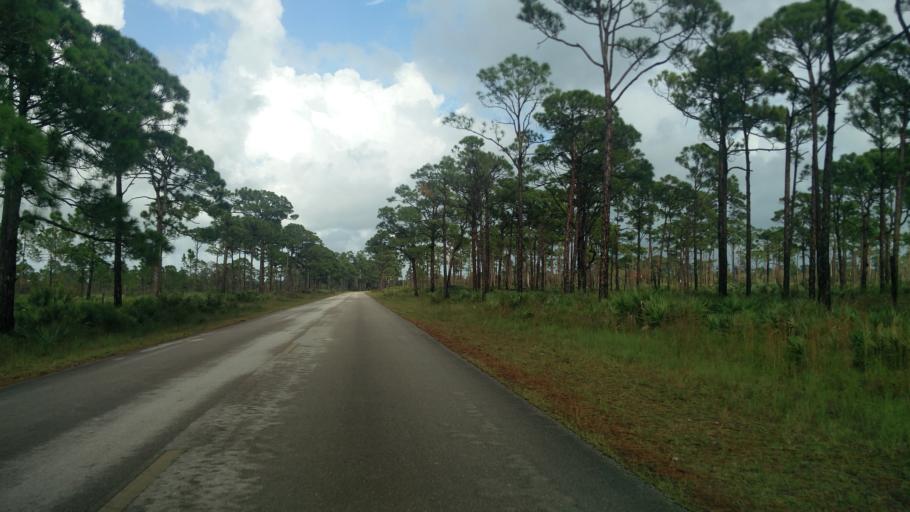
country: US
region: Florida
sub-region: Palm Beach County
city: Tequesta
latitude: 27.0093
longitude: -80.1249
